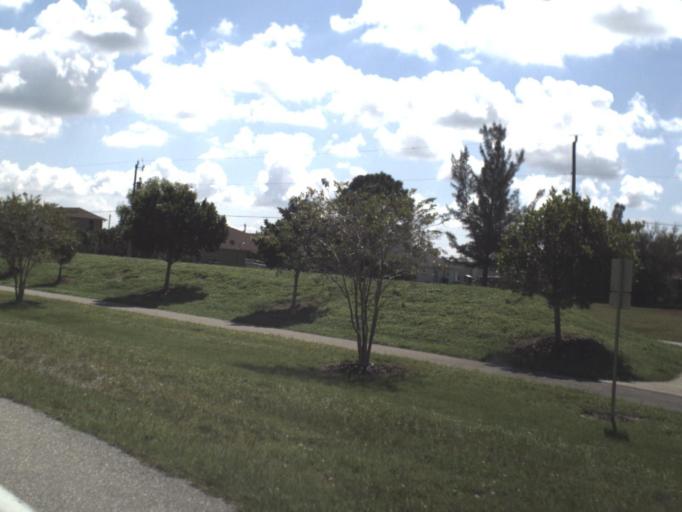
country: US
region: Florida
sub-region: Lee County
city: Pine Island Center
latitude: 26.6072
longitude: -82.0319
